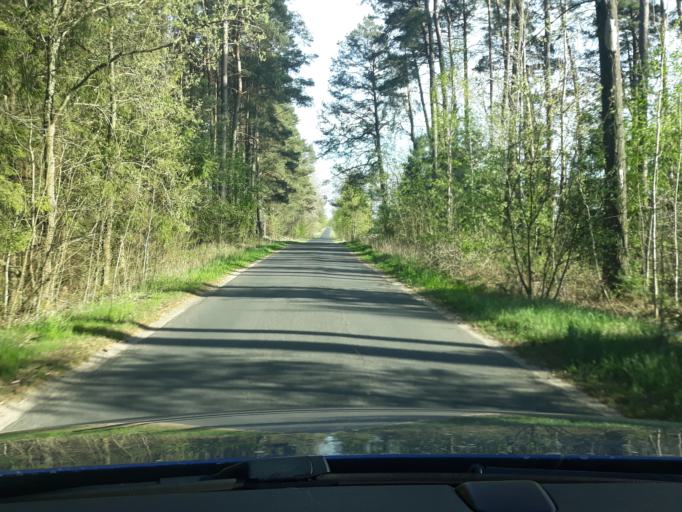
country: PL
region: Pomeranian Voivodeship
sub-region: Powiat czluchowski
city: Przechlewo
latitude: 53.8577
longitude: 17.3484
